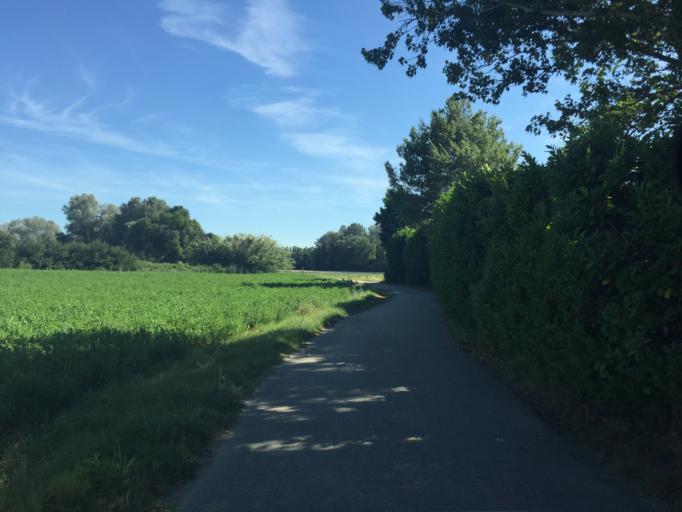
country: FR
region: Provence-Alpes-Cote d'Azur
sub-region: Departement du Vaucluse
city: Caderousse
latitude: 44.0888
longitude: 4.7652
